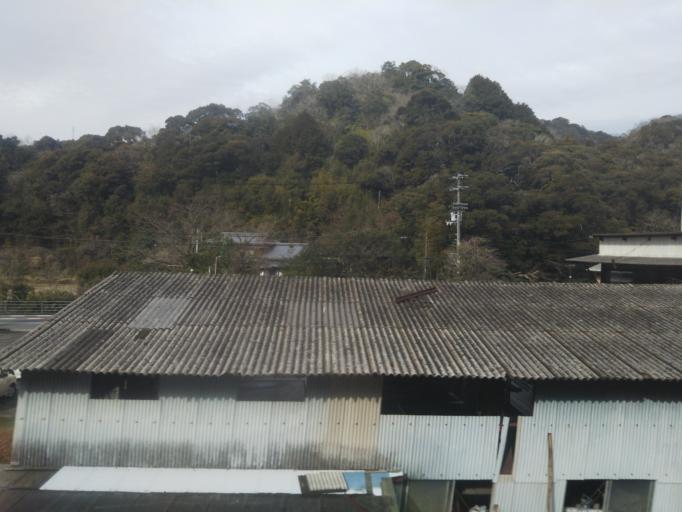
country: JP
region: Kochi
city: Nakamura
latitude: 32.9939
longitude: 132.9646
